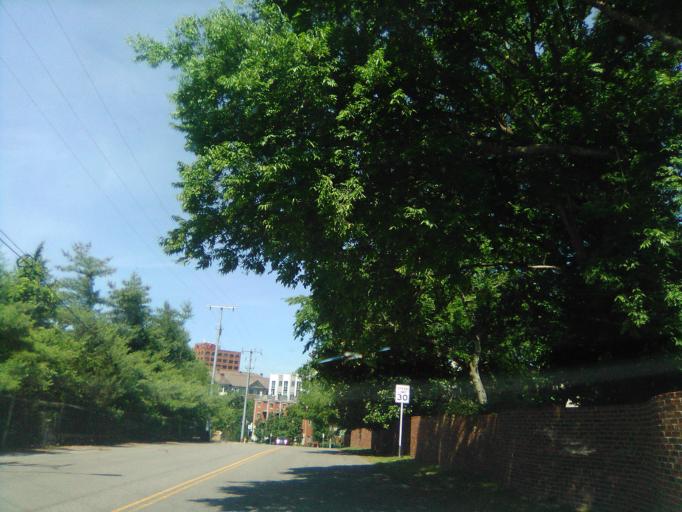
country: US
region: Tennessee
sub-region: Davidson County
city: Belle Meade
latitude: 36.1252
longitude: -86.8423
